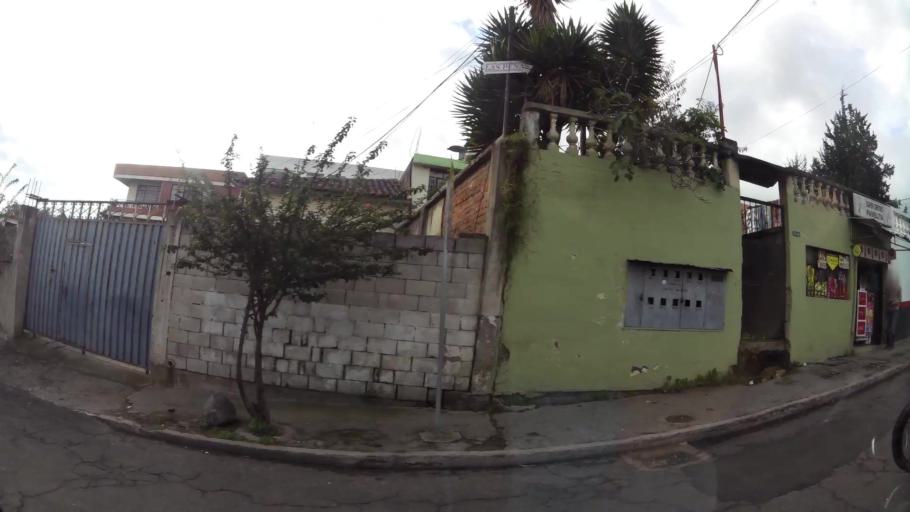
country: EC
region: Pichincha
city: Quito
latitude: -0.1439
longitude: -78.4668
